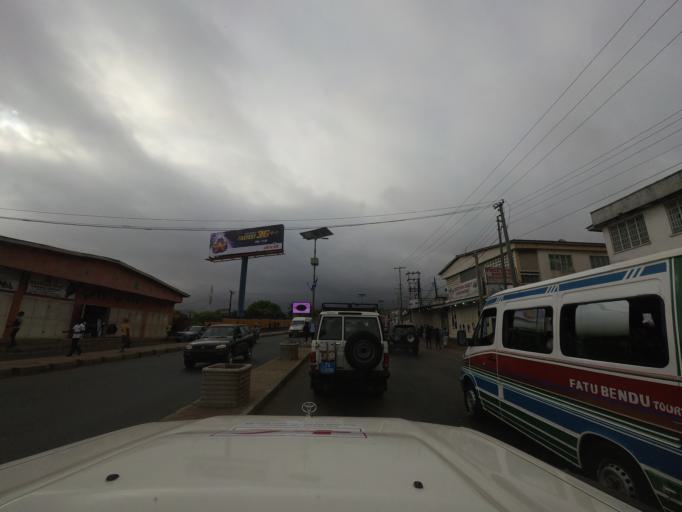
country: SL
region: Western Area
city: Freetown
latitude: 8.4845
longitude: -13.2597
